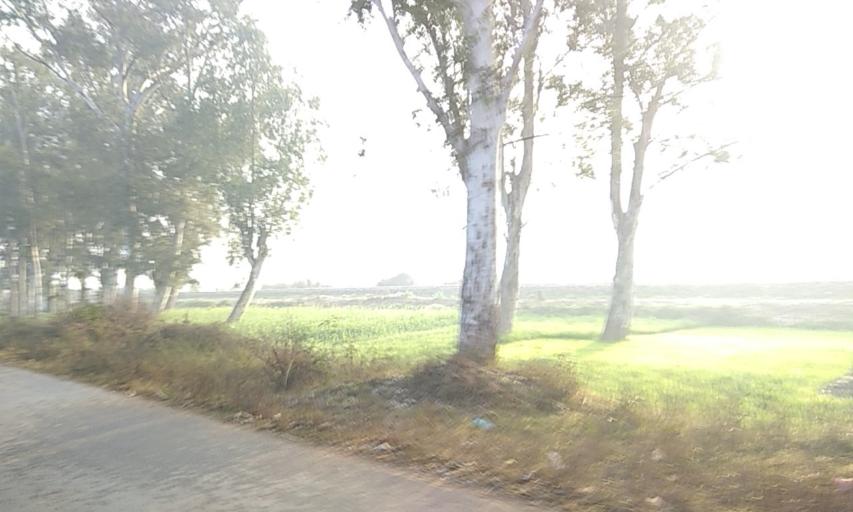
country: IN
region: Punjab
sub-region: Gurdaspur
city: Dhariwal
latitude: 31.9380
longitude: 75.3093
